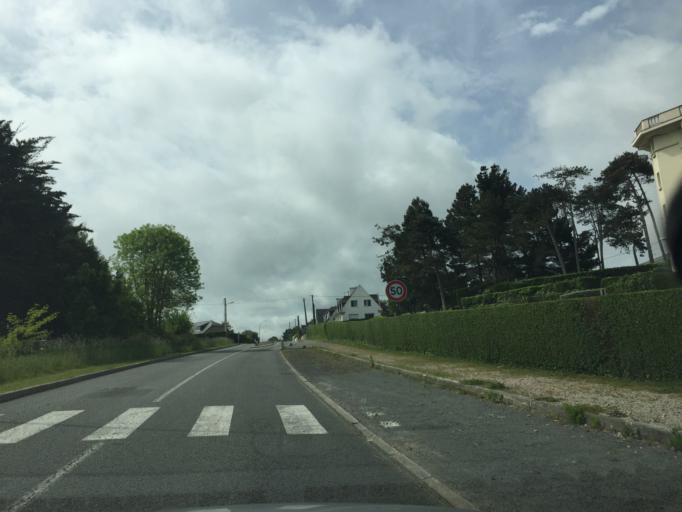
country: FR
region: Brittany
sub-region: Departement des Cotes-d'Armor
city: Saint-Cast-le-Guildo
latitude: 48.6117
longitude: -2.2441
